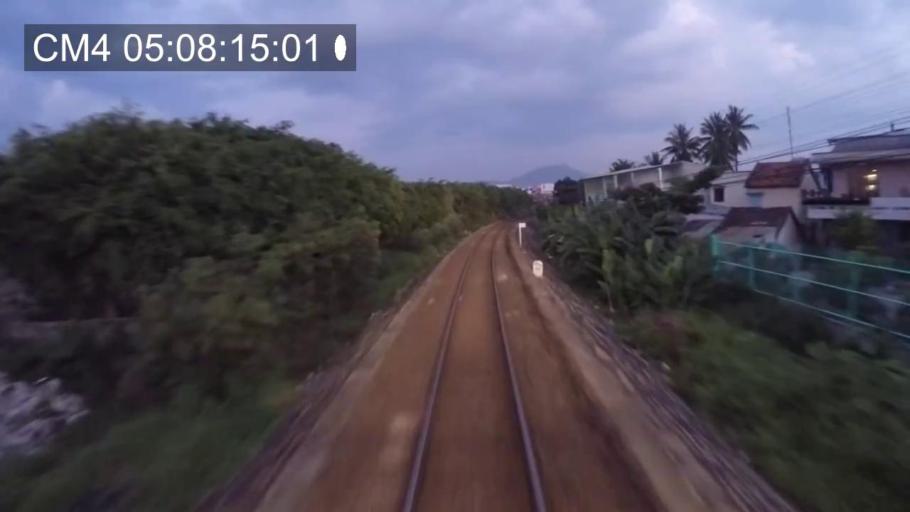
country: VN
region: Khanh Hoa
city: Nha Trang
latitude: 12.2912
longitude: 109.1861
